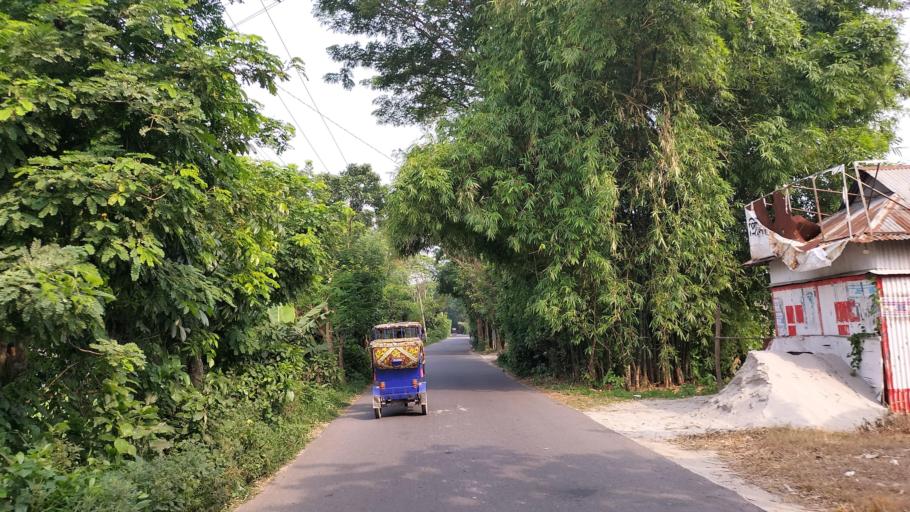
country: BD
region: Dhaka
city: Azimpur
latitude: 23.6781
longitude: 90.3159
